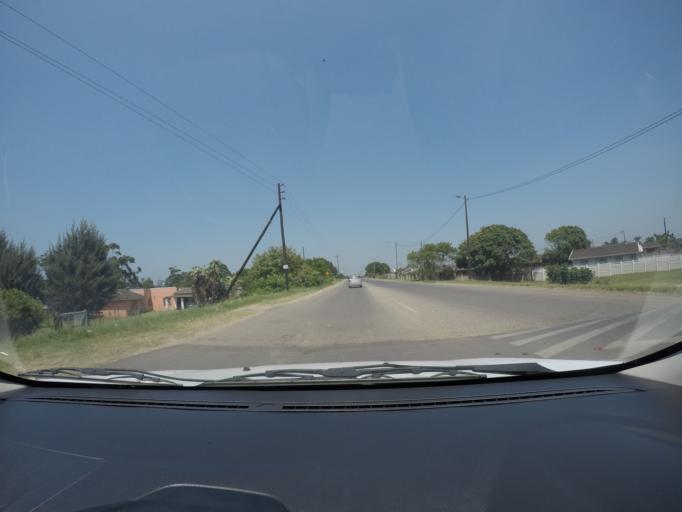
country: ZA
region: KwaZulu-Natal
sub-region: uThungulu District Municipality
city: eSikhawini
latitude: -28.8700
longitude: 31.9265
